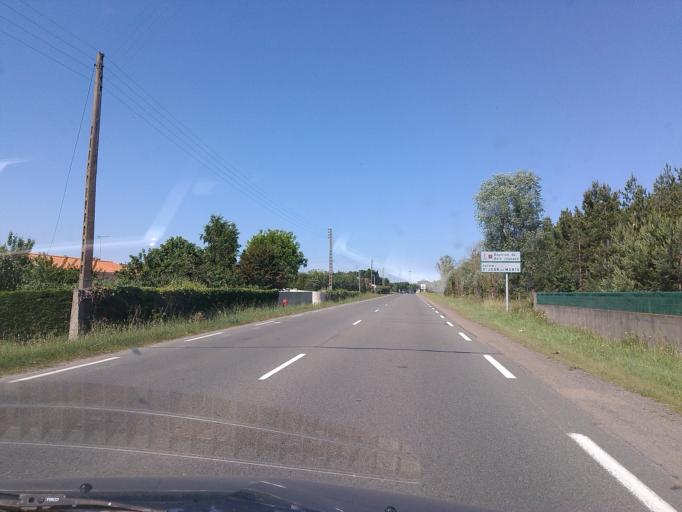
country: FR
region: Pays de la Loire
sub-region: Departement de la Vendee
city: Givrand
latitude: 46.6932
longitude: -1.8913
